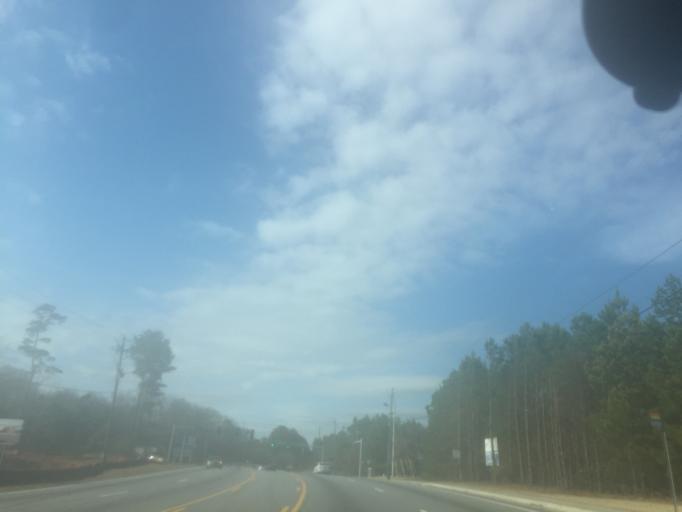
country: US
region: Georgia
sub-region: Clayton County
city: Riverdale
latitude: 33.5876
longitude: -84.4223
